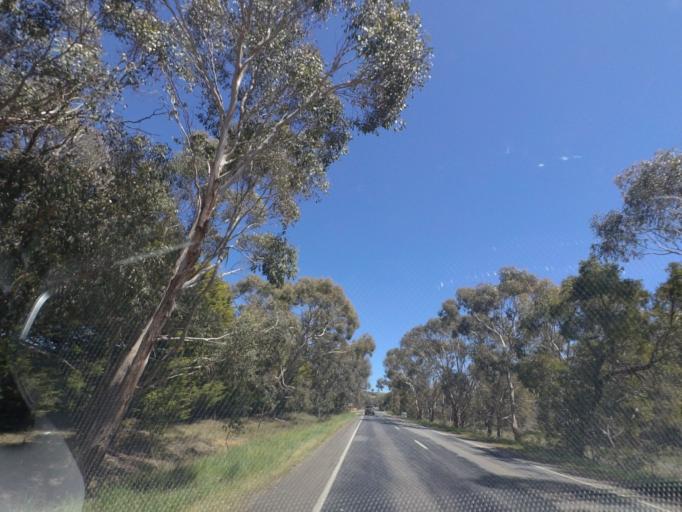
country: AU
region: Victoria
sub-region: Hume
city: Sunbury
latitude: -37.2989
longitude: 144.8194
